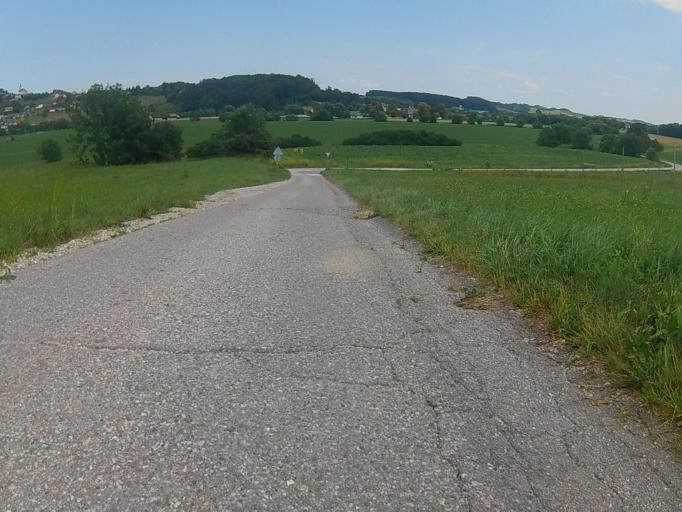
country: SI
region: Pesnica
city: Pesnica pri Mariboru
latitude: 46.6041
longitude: 15.6412
